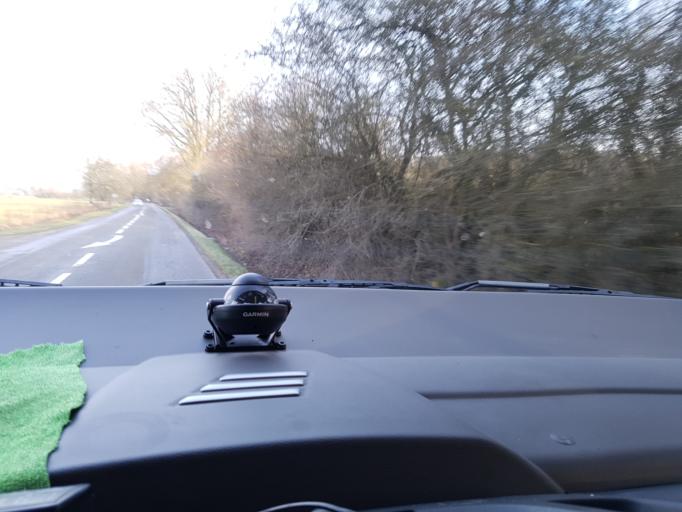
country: FR
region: Champagne-Ardenne
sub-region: Departement des Ardennes
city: Warcq
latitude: 49.7637
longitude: 4.6565
